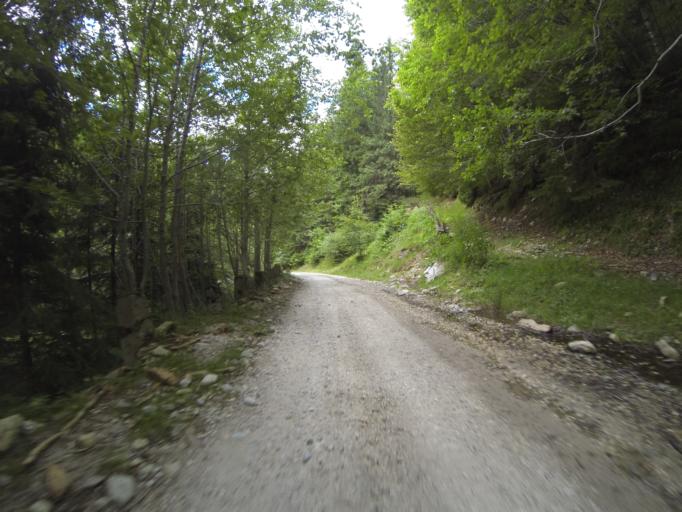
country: RO
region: Gorj
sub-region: Comuna Polovragi
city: Polovragi
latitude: 45.3213
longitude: 23.7942
